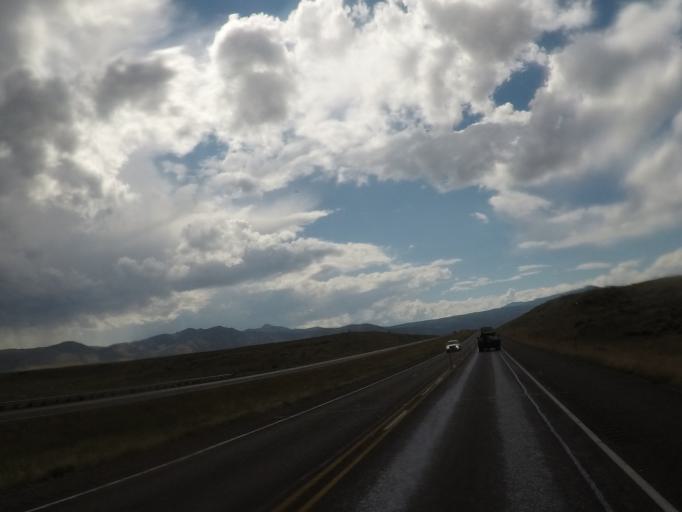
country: US
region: Montana
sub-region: Jefferson County
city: Whitehall
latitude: 45.8984
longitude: -112.2022
